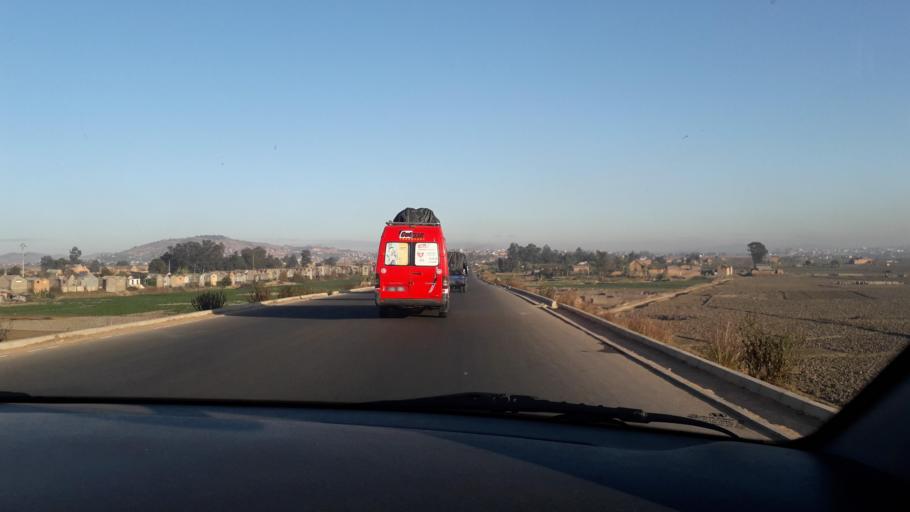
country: MG
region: Analamanga
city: Antananarivo
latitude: -18.8782
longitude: 47.4817
